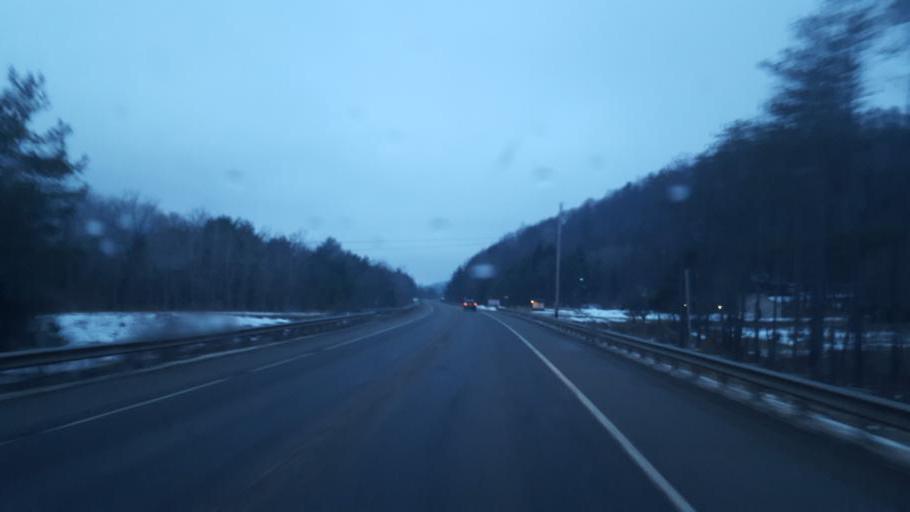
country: US
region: Pennsylvania
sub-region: Potter County
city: Coudersport
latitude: 41.7820
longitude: -78.1510
